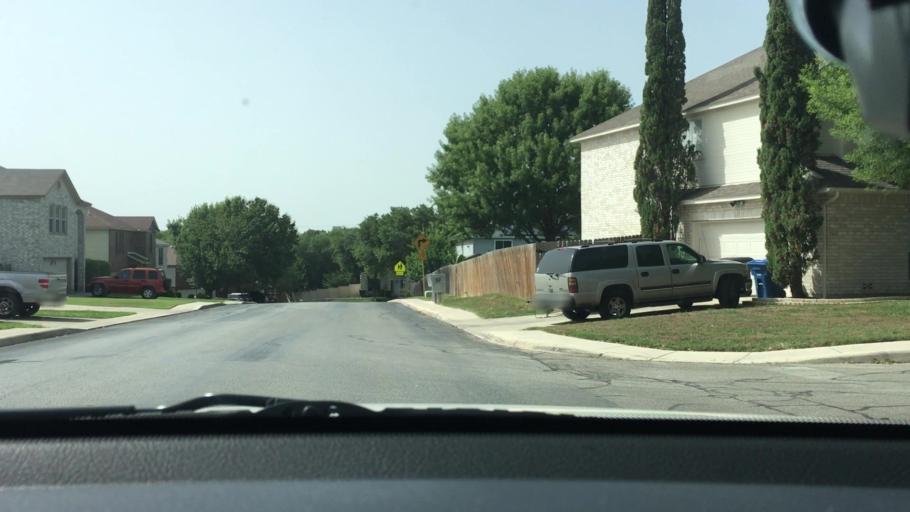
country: US
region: Texas
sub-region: Bexar County
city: Live Oak
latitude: 29.5794
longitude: -98.3840
